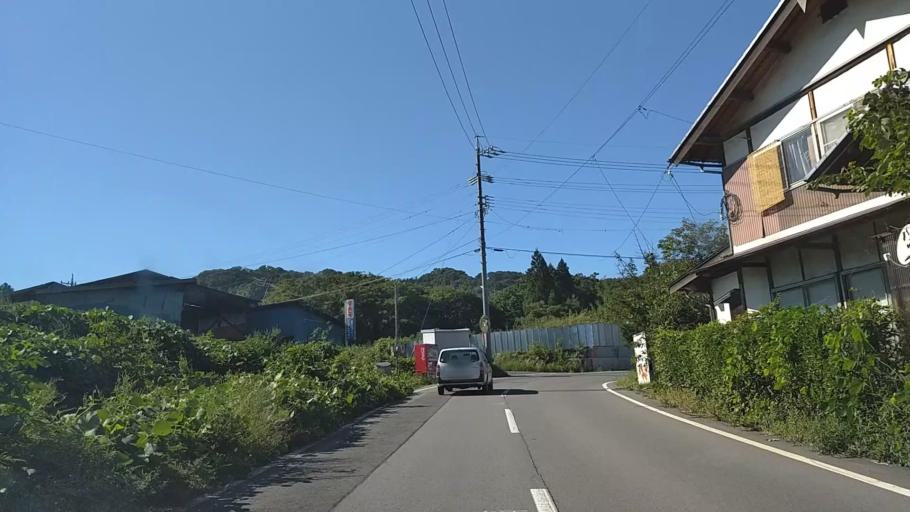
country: JP
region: Nagano
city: Nagano-shi
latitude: 36.5778
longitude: 138.1138
